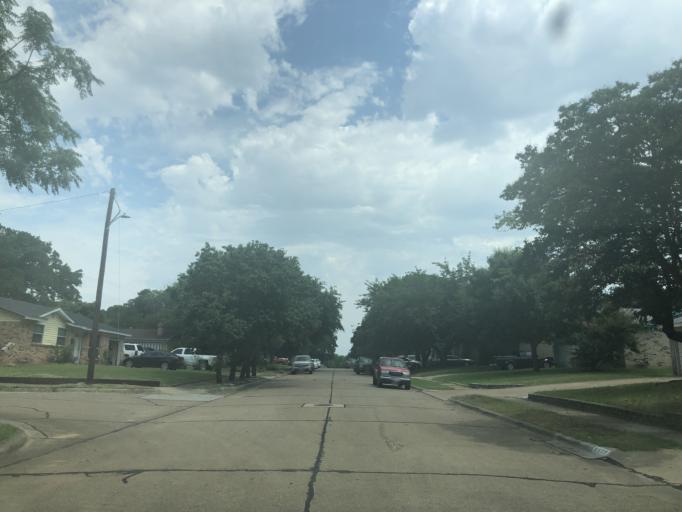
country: US
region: Texas
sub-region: Dallas County
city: Irving
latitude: 32.7910
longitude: -96.9390
